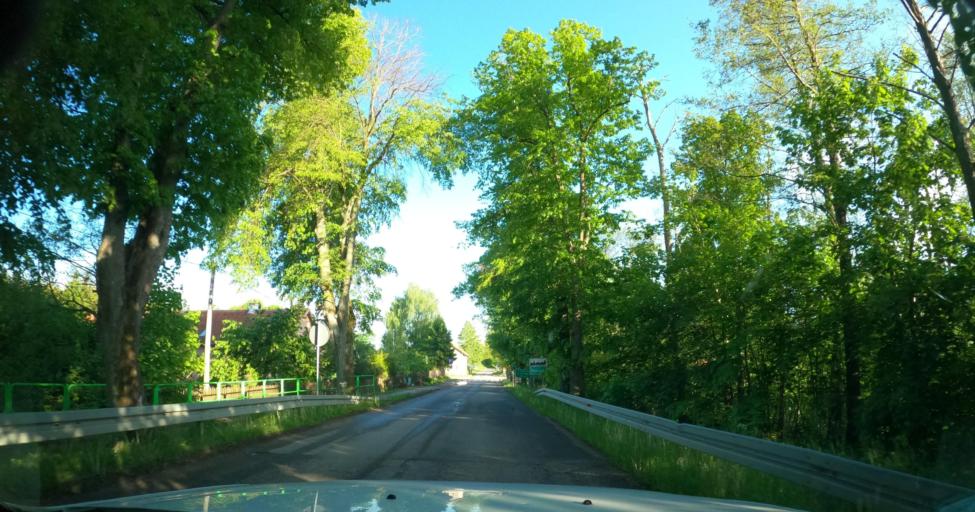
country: PL
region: Warmian-Masurian Voivodeship
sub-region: Powiat braniewski
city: Pieniezno
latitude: 54.2444
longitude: 20.0274
